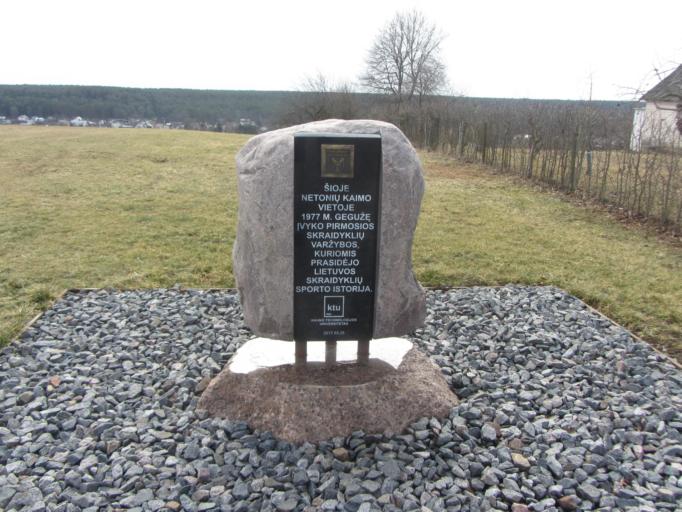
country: LT
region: Kauno apskritis
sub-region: Kauno rajonas
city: Akademija (Kaunas)
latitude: 54.9407
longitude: 23.7217
